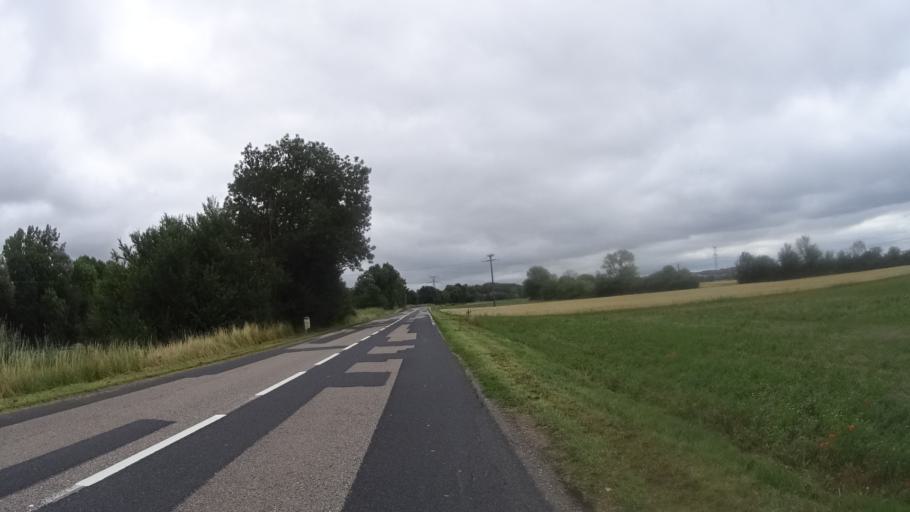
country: FR
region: Lorraine
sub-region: Departement de Meurthe-et-Moselle
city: Laneuveville-devant-Nancy
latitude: 48.6605
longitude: 6.2407
